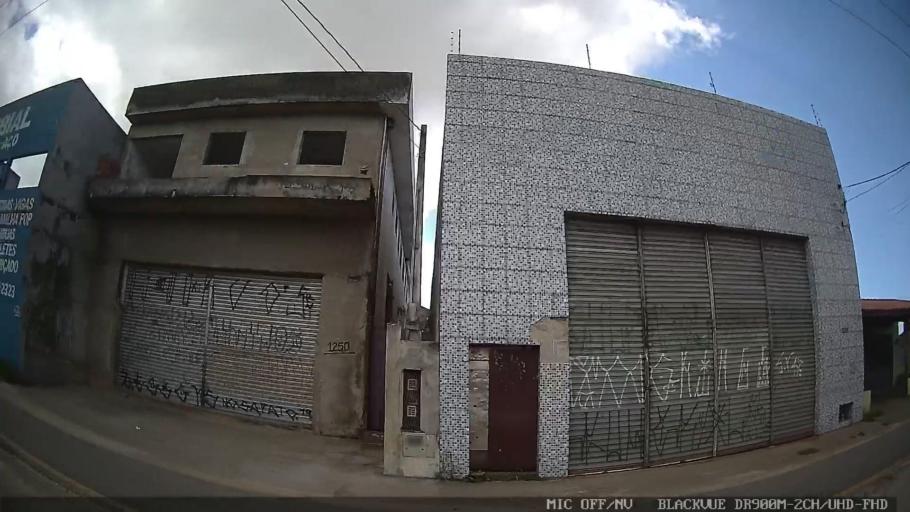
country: BR
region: Sao Paulo
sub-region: Peruibe
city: Peruibe
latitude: -24.3081
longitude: -47.0122
